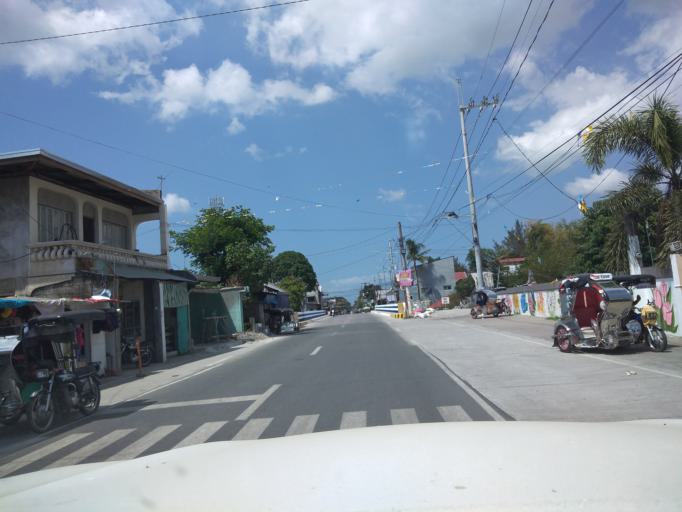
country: PH
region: Central Luzon
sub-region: Province of Pampanga
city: Bahay Pare
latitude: 15.0307
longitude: 120.8817
